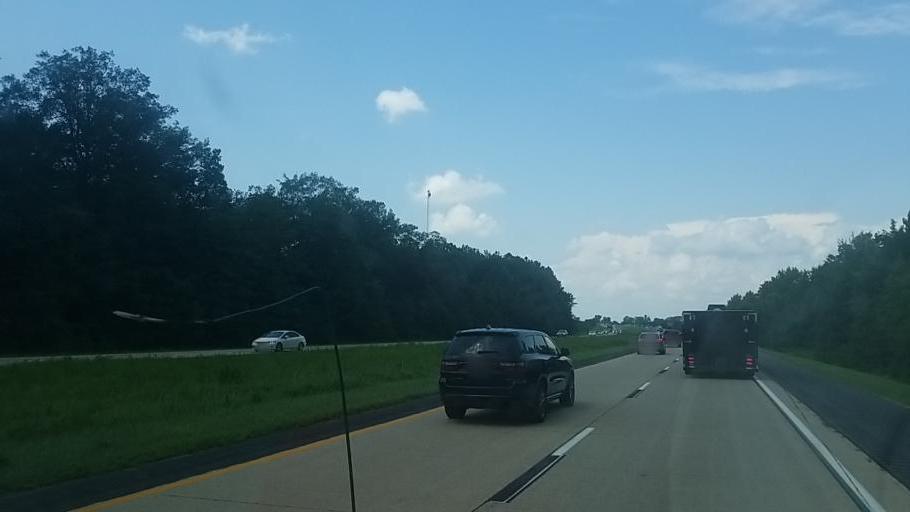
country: US
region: Delaware
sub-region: Kent County
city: Smyrna
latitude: 39.2652
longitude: -75.5791
